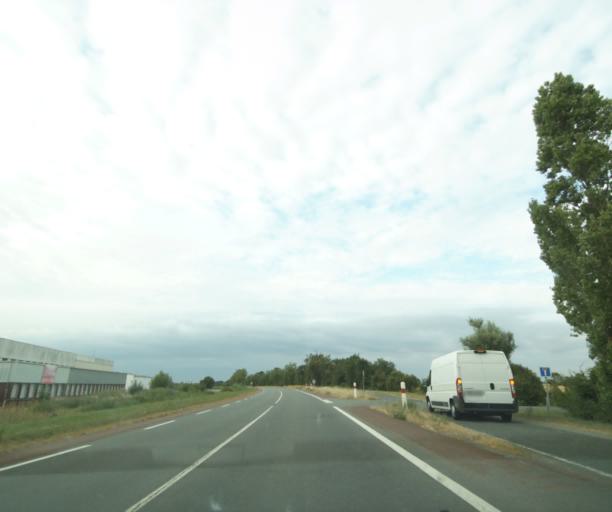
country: FR
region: Poitou-Charentes
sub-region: Departement de la Charente-Maritime
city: Marans
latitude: 46.2838
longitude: -0.9942
